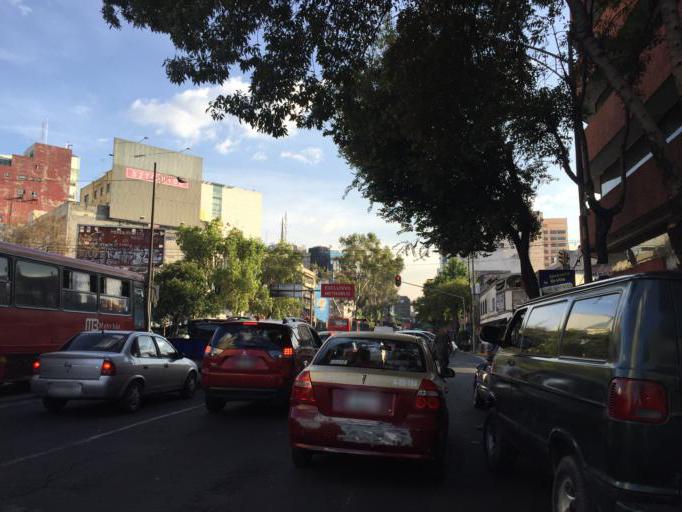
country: MX
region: Mexico City
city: Cuauhtemoc
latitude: 19.4347
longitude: -99.1580
